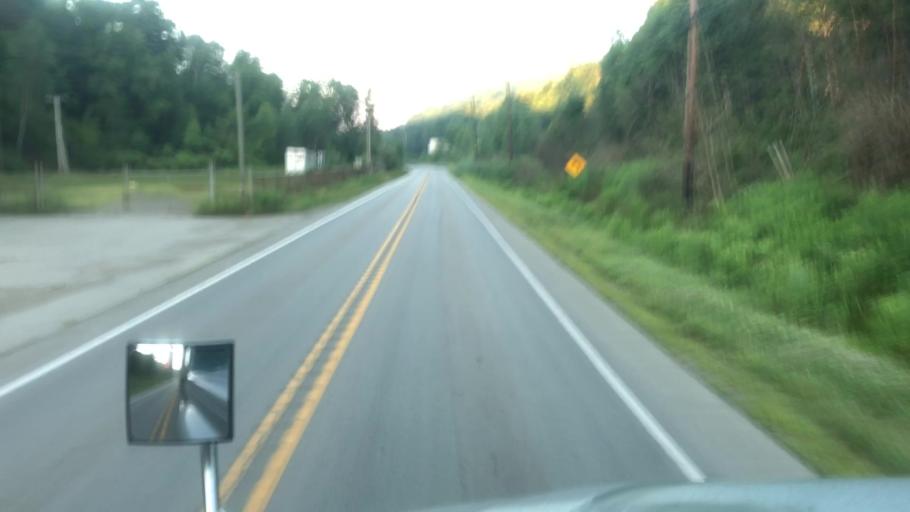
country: US
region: Pennsylvania
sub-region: Venango County
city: Hasson Heights
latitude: 41.4806
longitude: -79.6763
